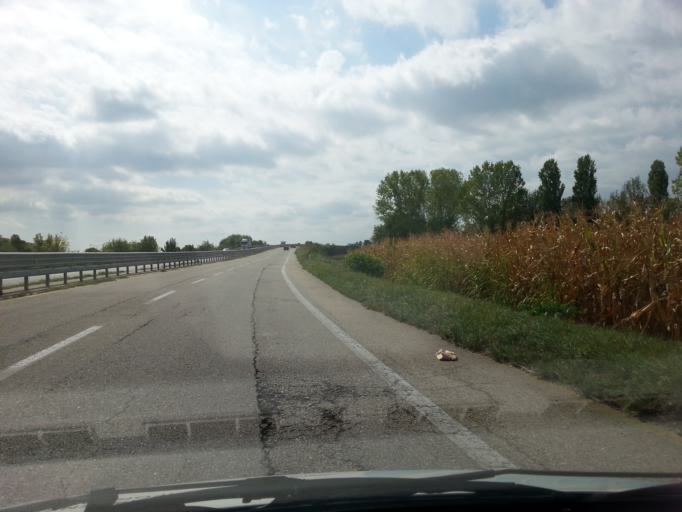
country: IT
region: Piedmont
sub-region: Provincia di Torino
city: Riva
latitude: 44.8996
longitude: 7.3606
